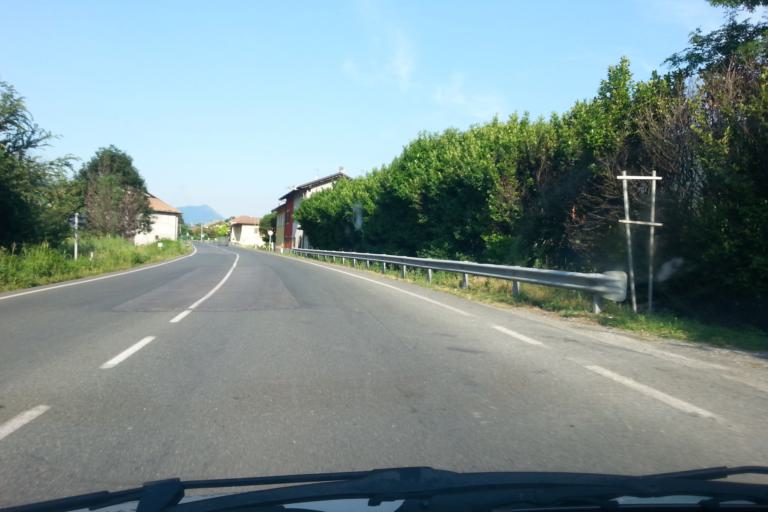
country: IT
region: Piedmont
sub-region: Provincia di Torino
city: Sant'Antonino di Susa
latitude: 45.1131
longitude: 7.2616
